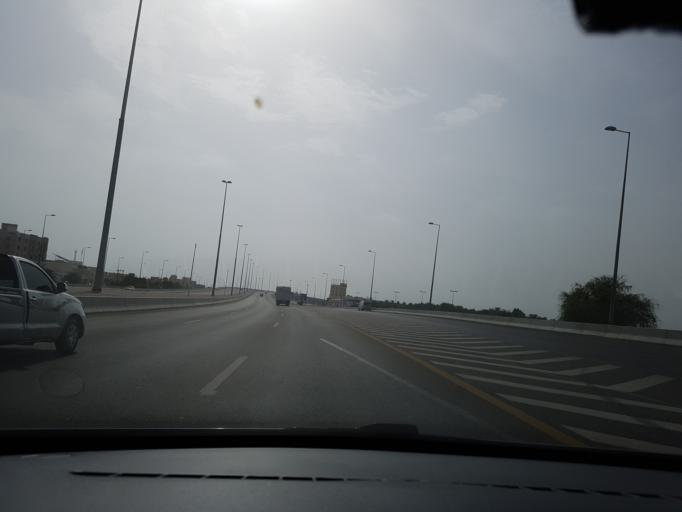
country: OM
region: Al Batinah
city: Al Sohar
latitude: 24.3435
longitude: 56.7223
